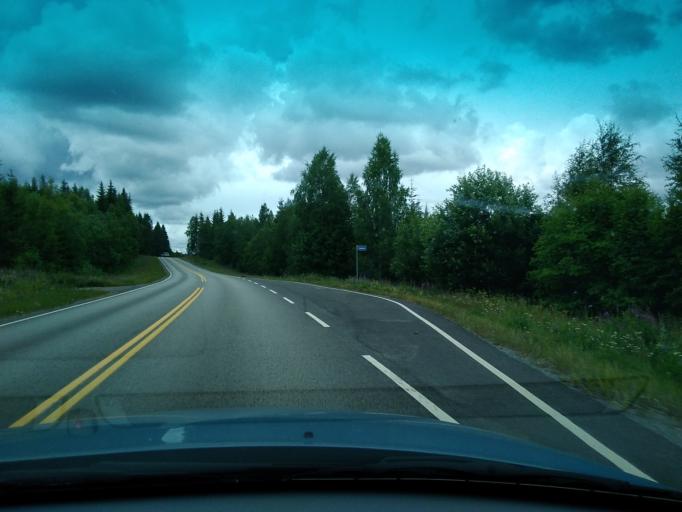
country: FI
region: Central Finland
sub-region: Saarijaervi-Viitasaari
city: Pylkoenmaeki
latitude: 62.6499
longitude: 24.9898
